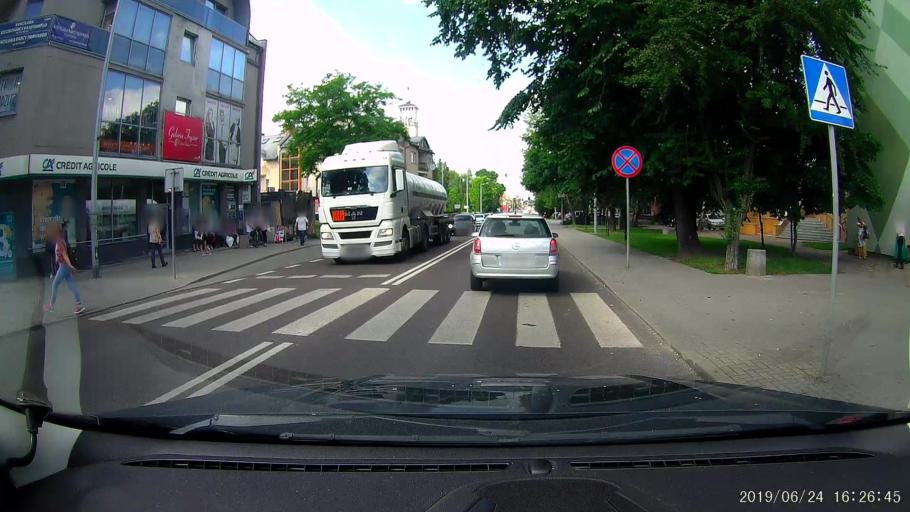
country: PL
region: Lublin Voivodeship
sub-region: Powiat tomaszowski
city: Tomaszow Lubelski
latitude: 50.4481
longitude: 23.4166
